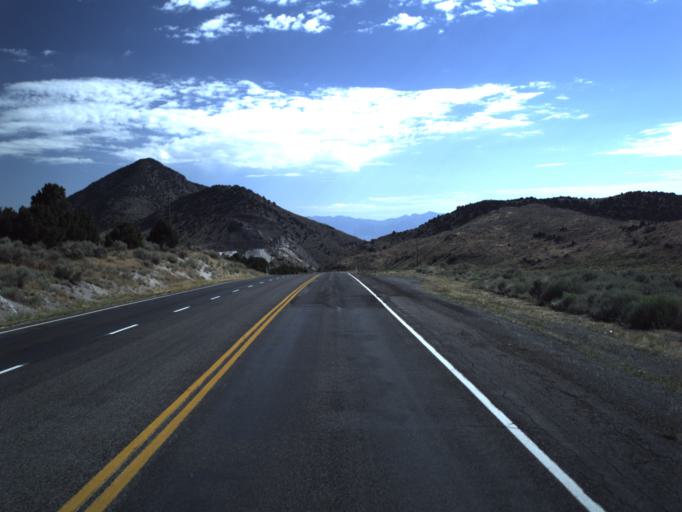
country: US
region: Utah
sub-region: Utah County
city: Genola
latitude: 39.9628
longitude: -112.0978
